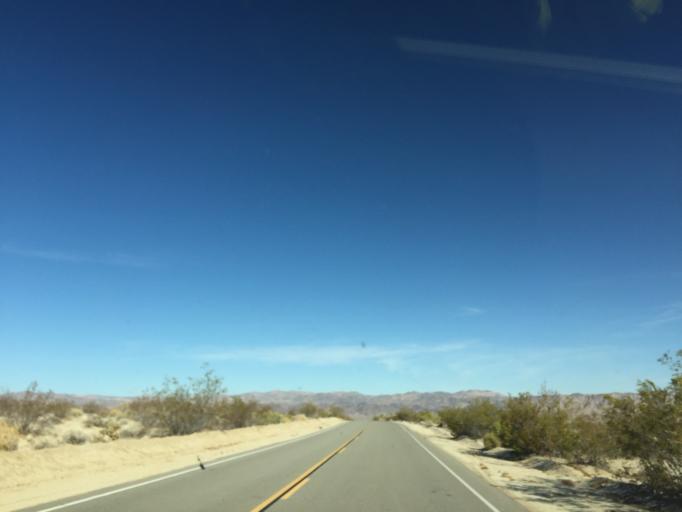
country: US
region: California
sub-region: San Bernardino County
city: Twentynine Palms
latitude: 33.8762
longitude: -115.8100
